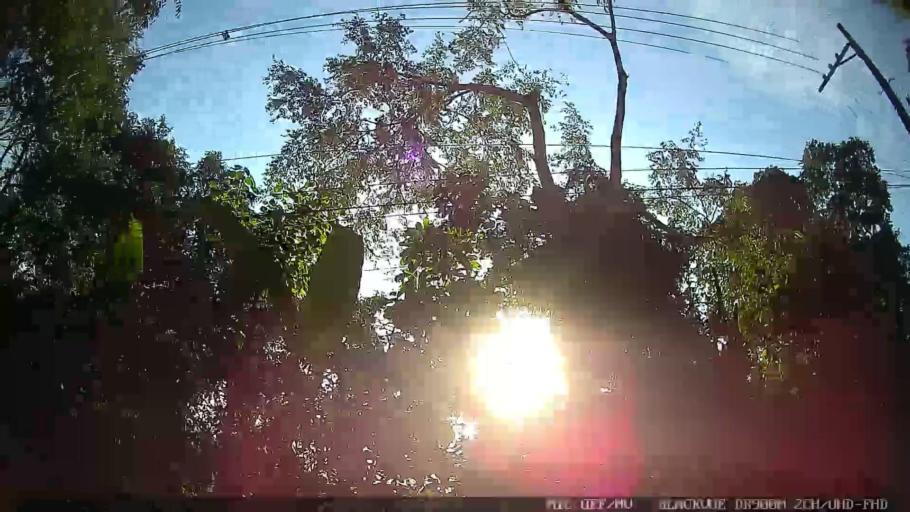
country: BR
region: Sao Paulo
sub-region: Guaruja
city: Guaruja
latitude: -23.9819
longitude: -46.2583
